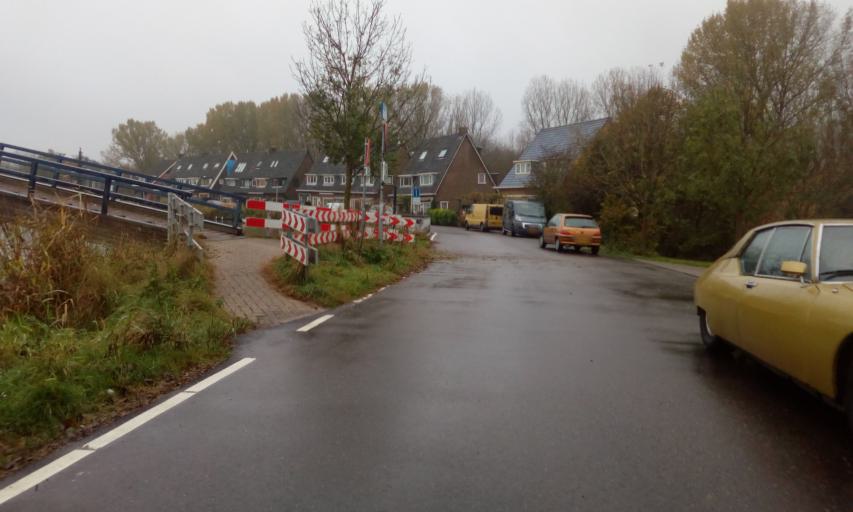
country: NL
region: South Holland
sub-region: Gemeente Lansingerland
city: Bergschenhoek
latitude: 51.9638
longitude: 4.5215
